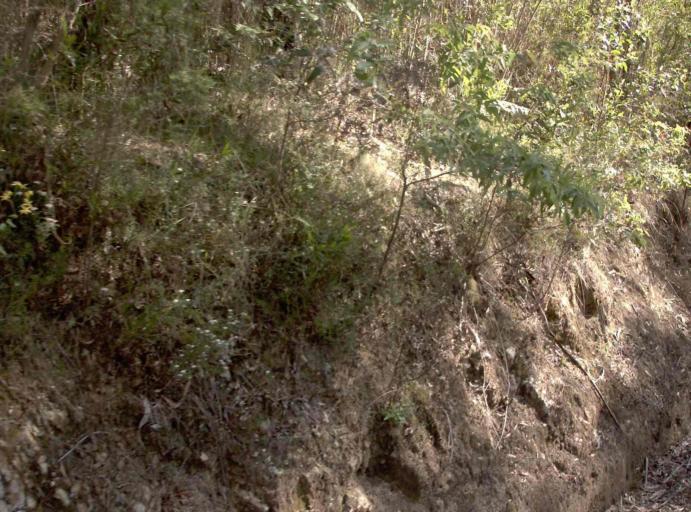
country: AU
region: Victoria
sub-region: East Gippsland
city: Lakes Entrance
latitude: -37.5151
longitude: 148.5475
